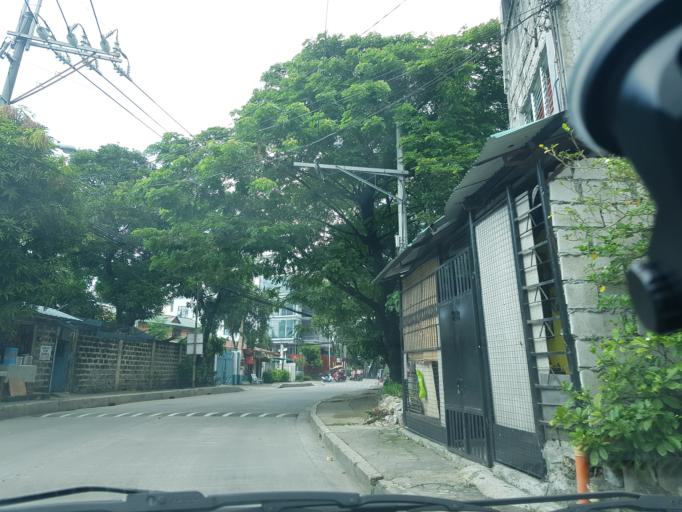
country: PH
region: Metro Manila
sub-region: Pasig
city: Pasig City
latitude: 14.5826
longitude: 121.0913
